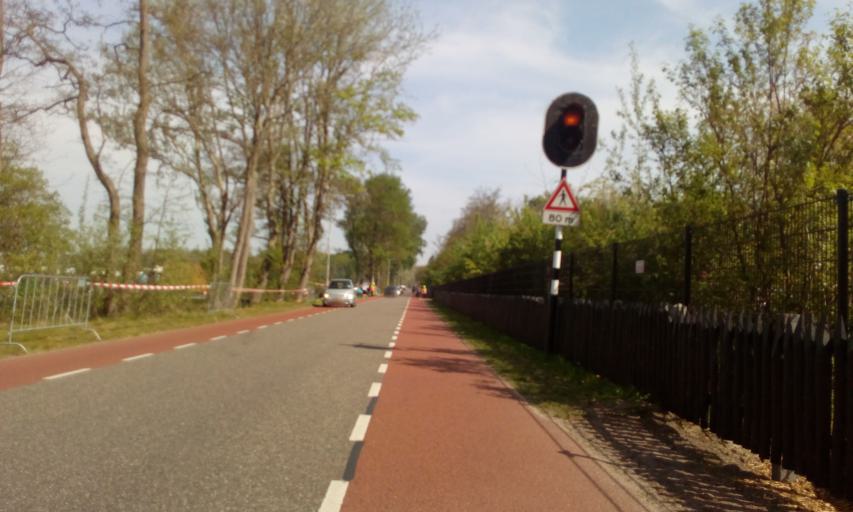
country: NL
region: South Holland
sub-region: Gemeente Lisse
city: Lisse
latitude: 52.2711
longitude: 4.5436
